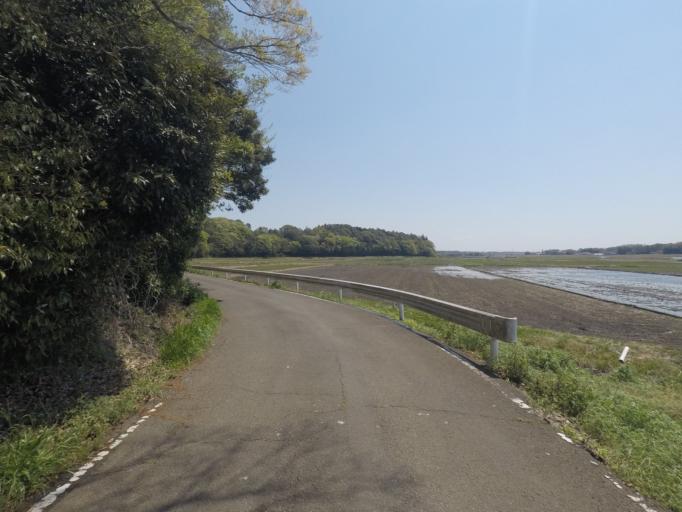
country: JP
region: Ibaraki
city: Ushiku
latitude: 36.0004
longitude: 140.0989
